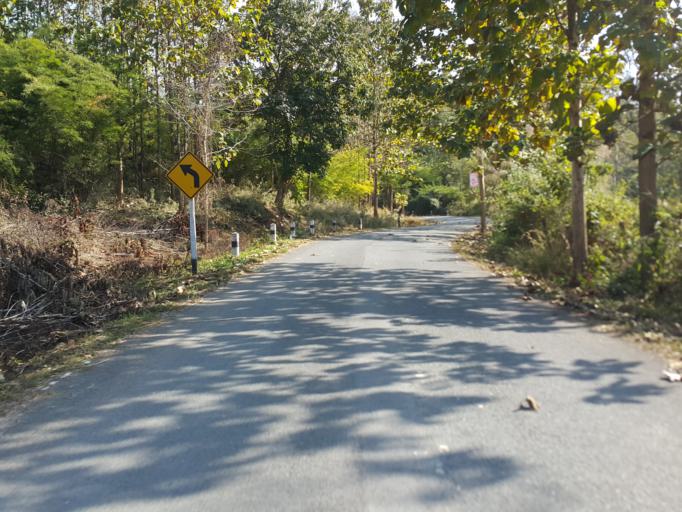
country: TH
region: Chiang Mai
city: Mae On
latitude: 18.7943
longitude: 99.2321
